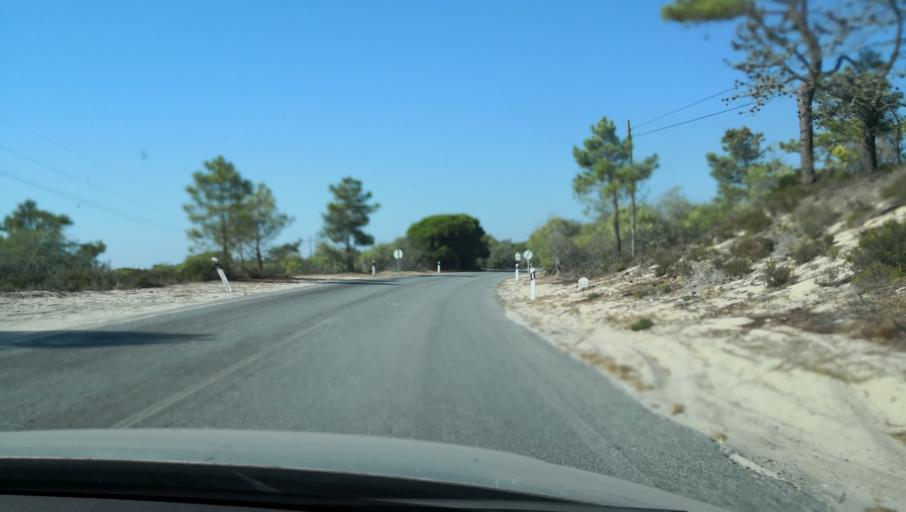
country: PT
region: Setubal
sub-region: Setubal
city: Setubal
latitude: 38.3865
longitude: -8.7997
